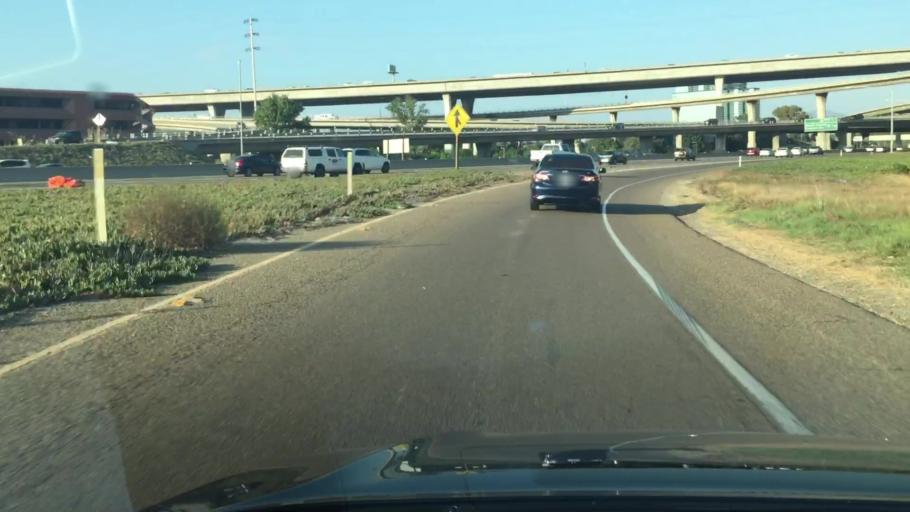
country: US
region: California
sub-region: San Diego County
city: San Diego
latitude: 32.7706
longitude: -117.1351
